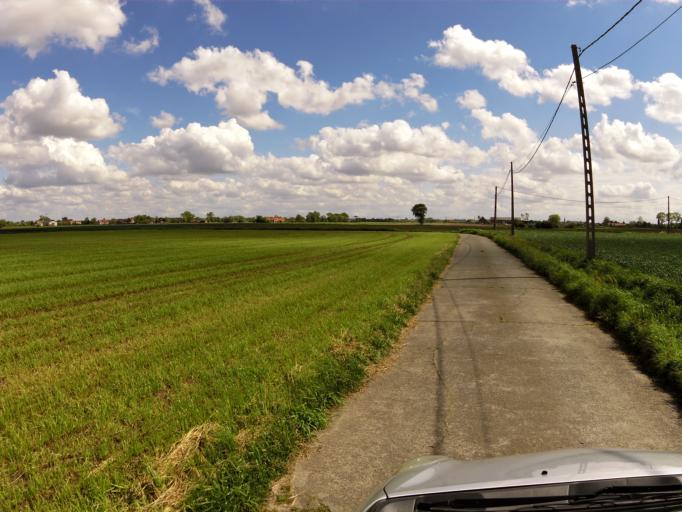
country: BE
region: Flanders
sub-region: Provincie West-Vlaanderen
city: Koekelare
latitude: 51.1186
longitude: 2.9645
